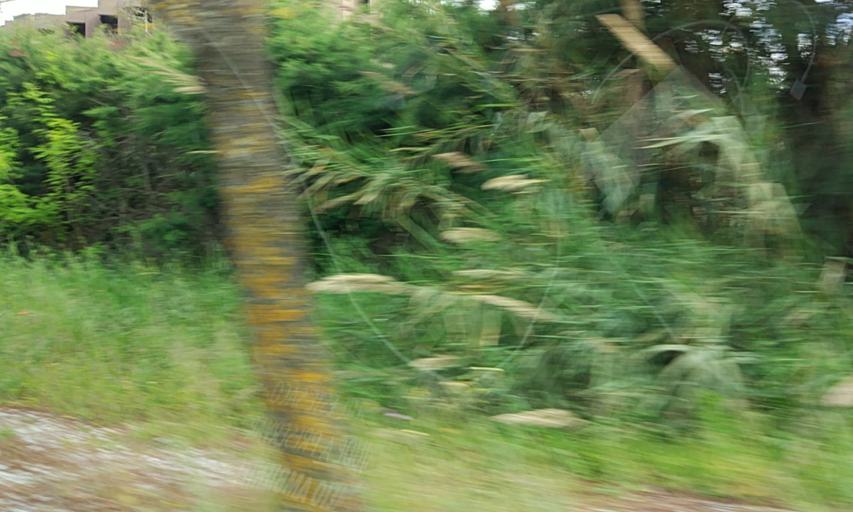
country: PT
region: Evora
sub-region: Evora
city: Evora
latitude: 38.5675
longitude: -7.9384
